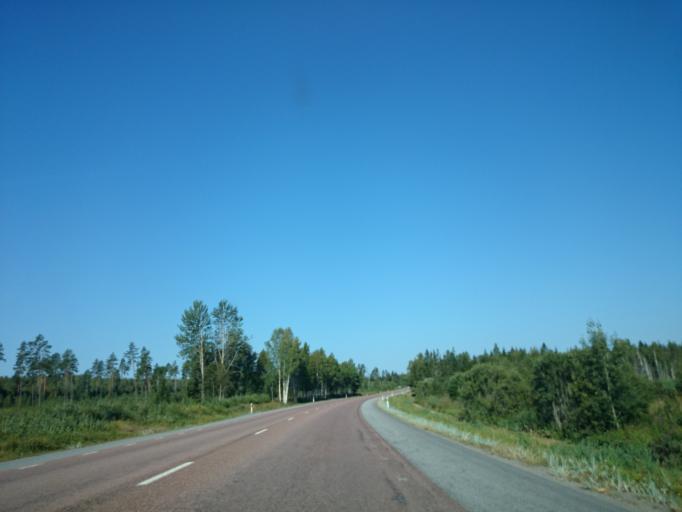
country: SE
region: Gaevleborg
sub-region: Hudiksvalls Kommun
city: Sorforsa
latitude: 61.7148
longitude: 17.0398
